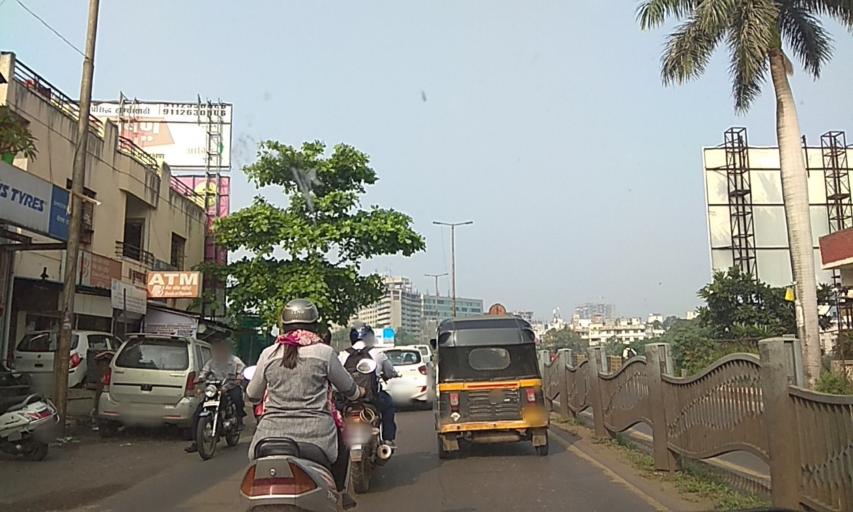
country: IN
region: Maharashtra
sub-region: Pune Division
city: Pune
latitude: 18.5047
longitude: 73.8376
